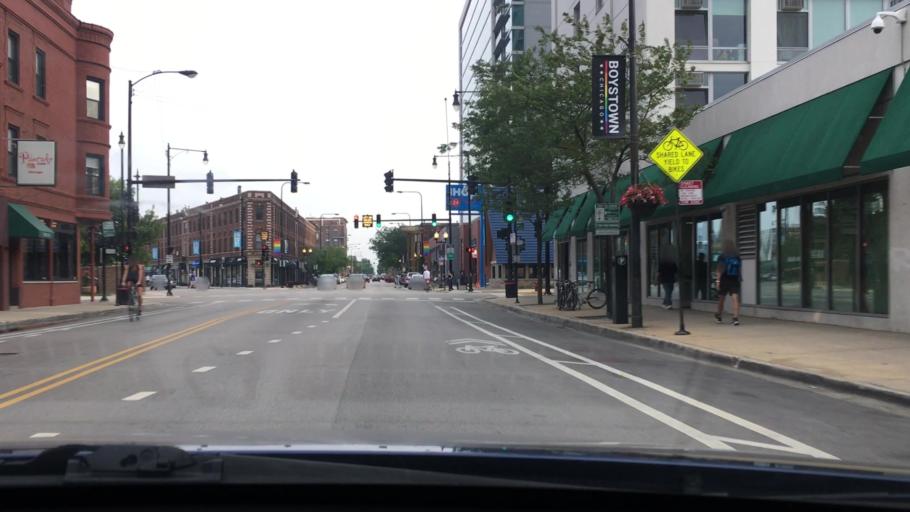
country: US
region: Illinois
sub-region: Cook County
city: Lincolnwood
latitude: 41.9517
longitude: -87.6497
